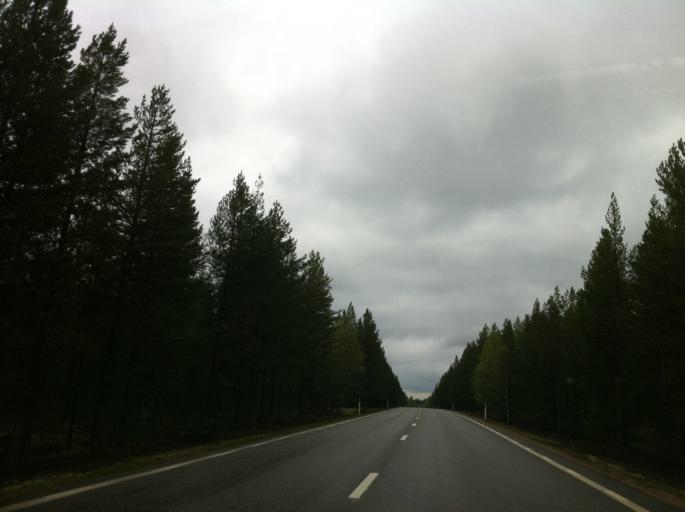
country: SE
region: Jaemtland
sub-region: Harjedalens Kommun
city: Sveg
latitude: 62.0590
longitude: 14.2928
